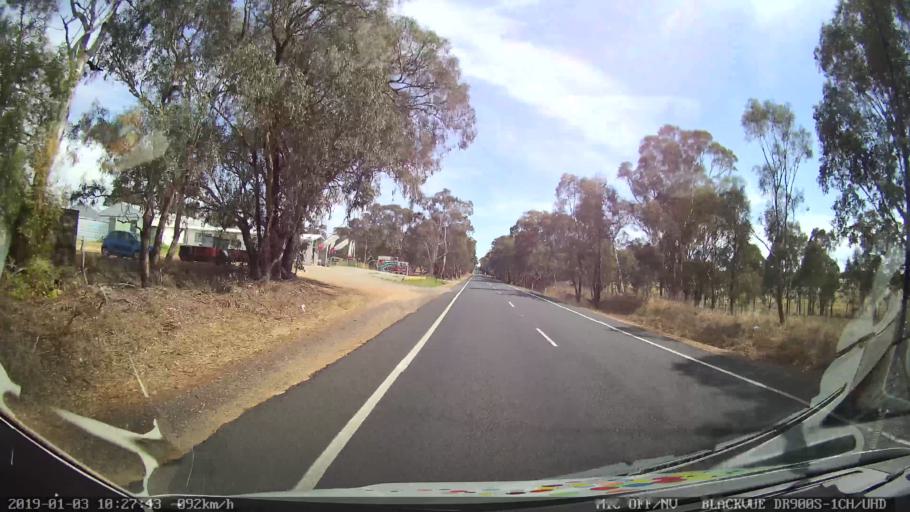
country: AU
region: New South Wales
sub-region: Young
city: Young
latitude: -34.3980
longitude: 148.2586
